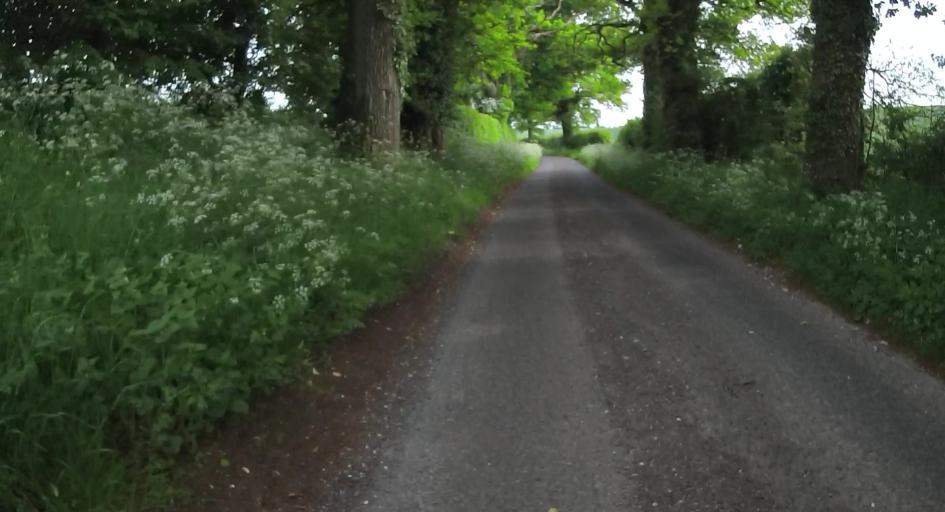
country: GB
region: England
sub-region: Hampshire
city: Overton
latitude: 51.2752
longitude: -1.2531
